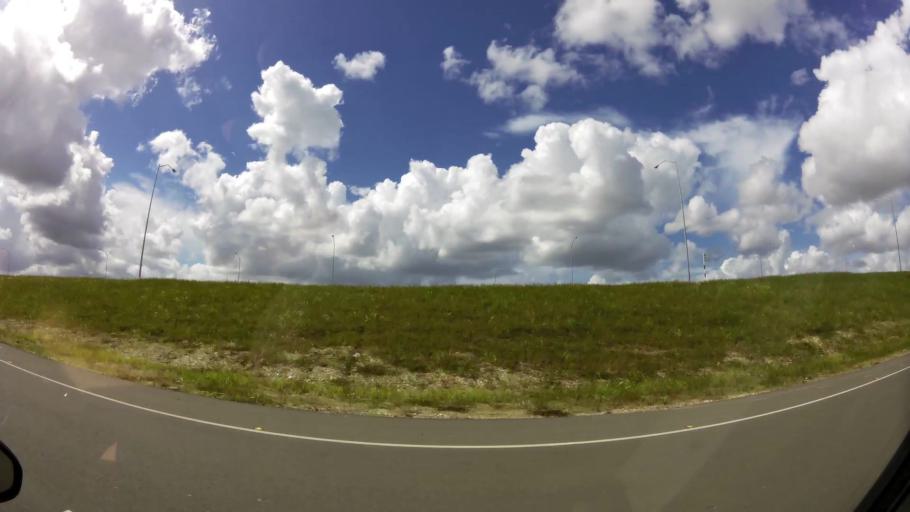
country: TT
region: Penal/Debe
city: Debe
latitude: 10.2154
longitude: -61.4558
